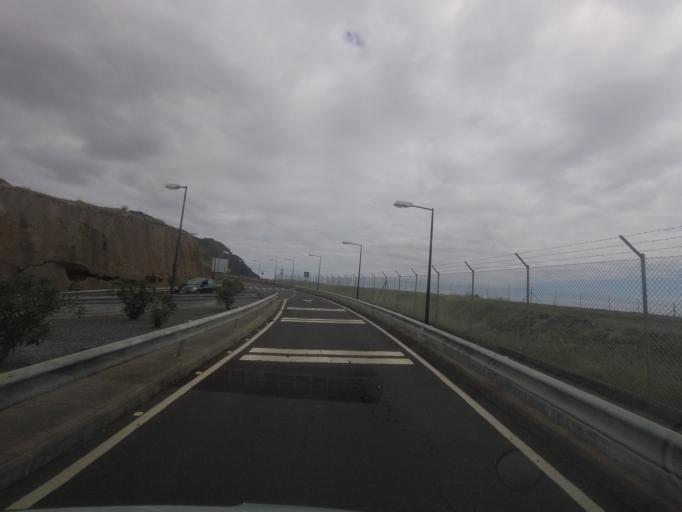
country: PT
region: Madeira
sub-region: Machico
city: Machico
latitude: 32.7090
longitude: -16.7620
